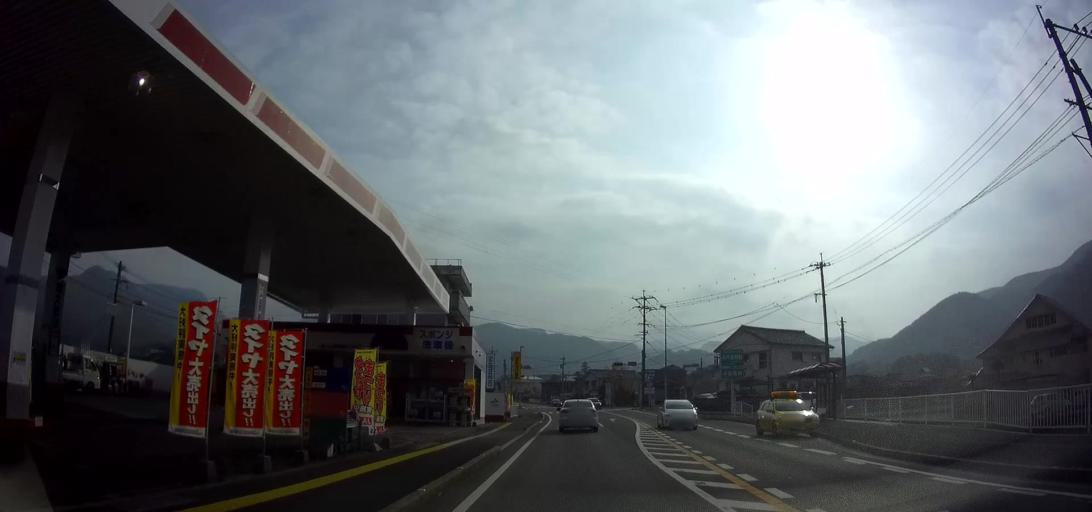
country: JP
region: Nagasaki
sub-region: Isahaya-shi
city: Isahaya
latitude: 32.7865
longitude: 130.1962
